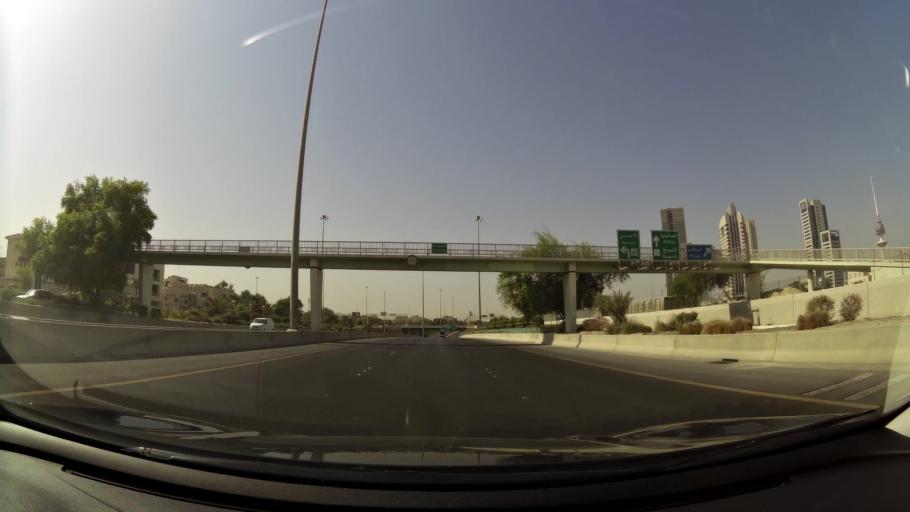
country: KW
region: Al Asimah
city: Ad Dasmah
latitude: 29.3628
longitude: 47.9894
